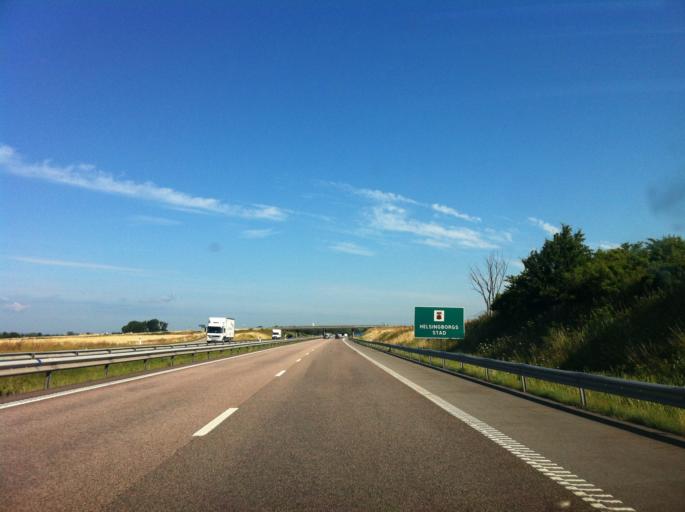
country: SE
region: Skane
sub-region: Helsingborg
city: Glumslov
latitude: 55.9616
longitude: 12.7995
